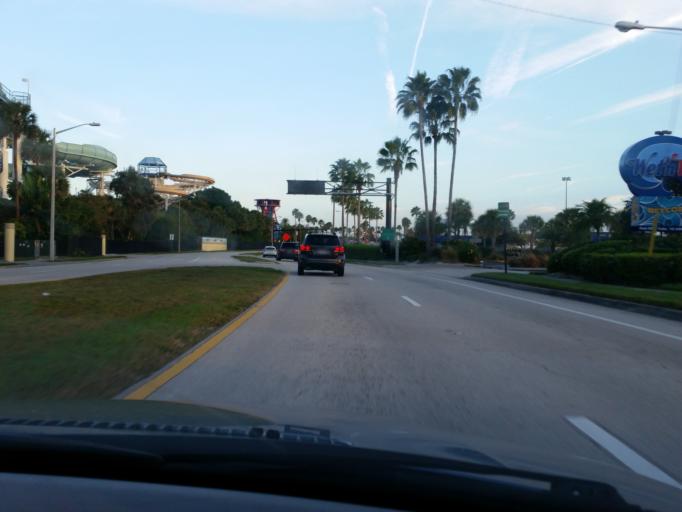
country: US
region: Florida
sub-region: Orange County
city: Tangelo Park
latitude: 28.4598
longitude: -81.4637
